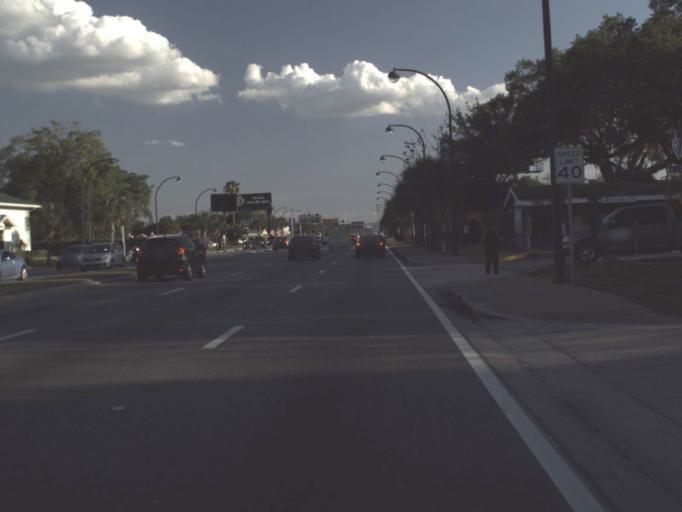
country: US
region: Florida
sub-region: Orange County
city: Holden Heights
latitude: 28.4894
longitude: -81.3969
